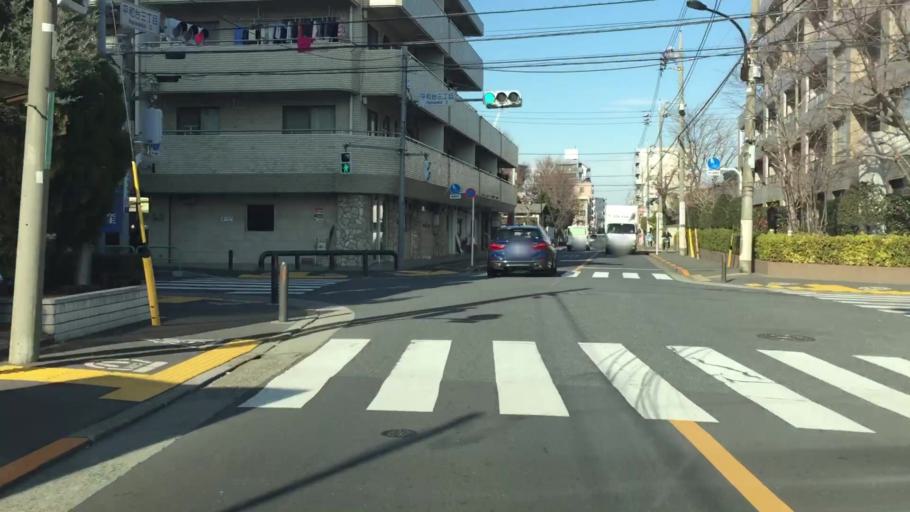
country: JP
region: Saitama
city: Wako
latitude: 35.7582
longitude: 139.6607
